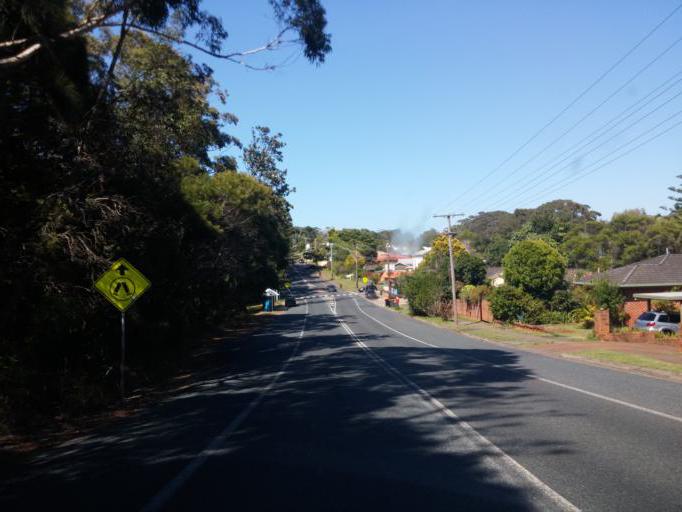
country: AU
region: New South Wales
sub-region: Port Macquarie-Hastings
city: Port Macquarie
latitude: -31.4586
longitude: 152.9298
